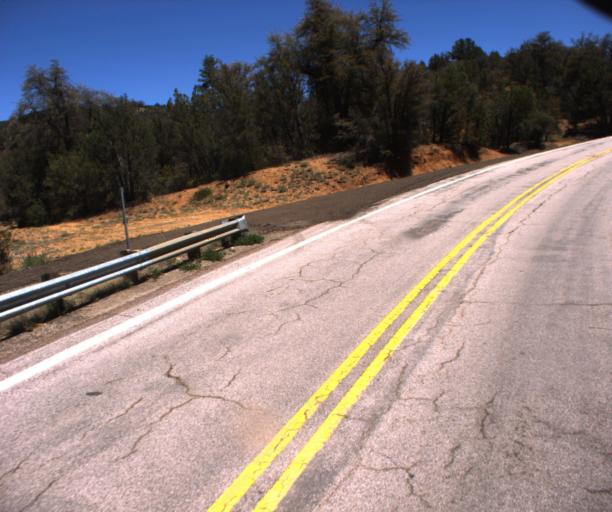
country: US
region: Arizona
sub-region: Yavapai County
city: Prescott
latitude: 34.4437
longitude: -112.5480
